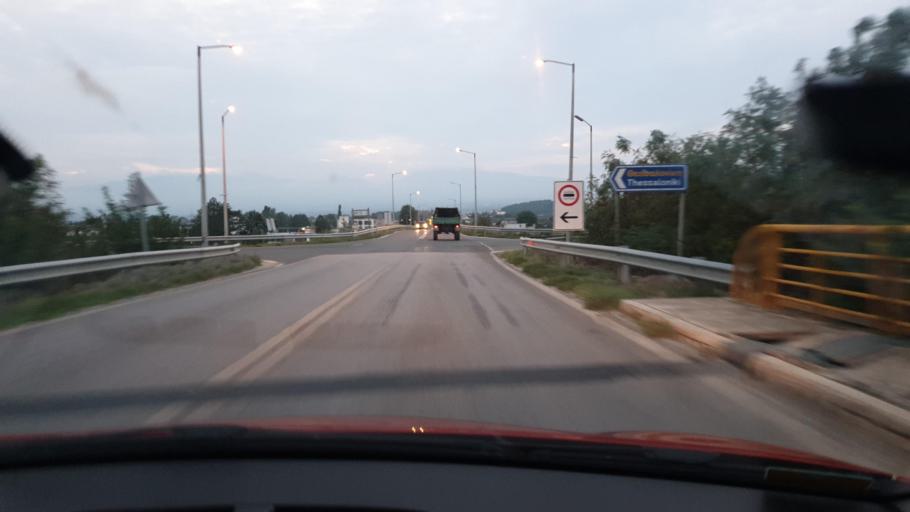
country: GR
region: Central Macedonia
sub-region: Nomos Kilkis
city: Polykastro
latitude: 40.9908
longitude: 22.6038
